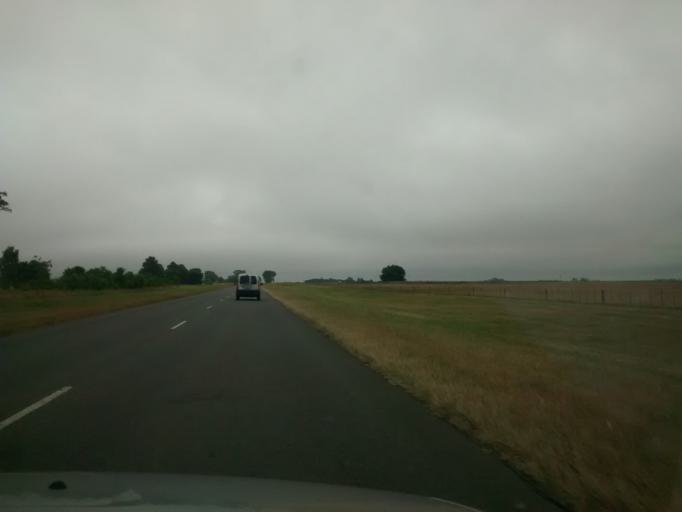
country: AR
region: Buenos Aires
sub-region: Partido de Ayacucho
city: Ayacucho
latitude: -37.2404
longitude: -58.4905
